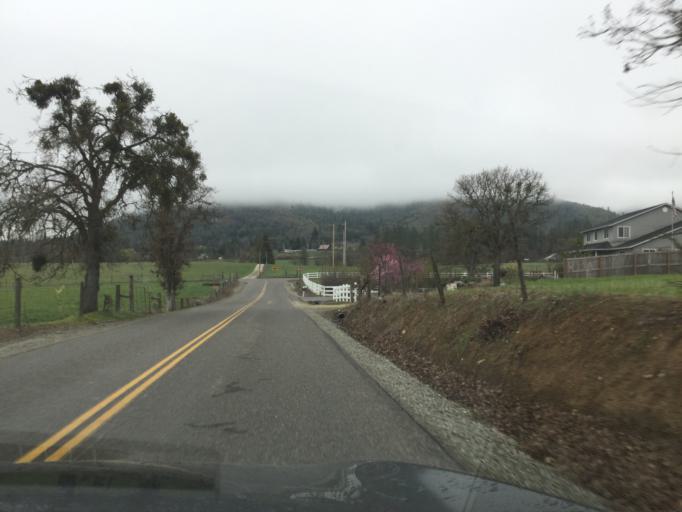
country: US
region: Oregon
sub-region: Jackson County
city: Central Point
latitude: 42.3916
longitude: -122.9686
